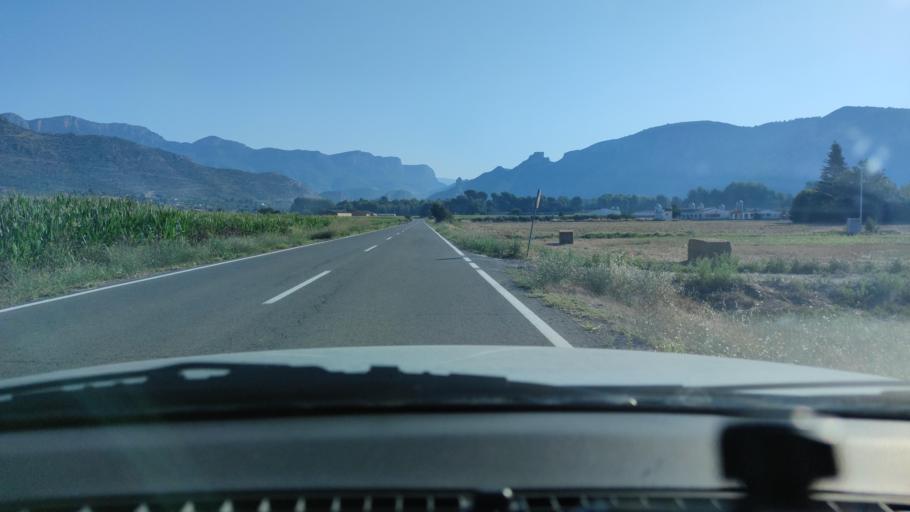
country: ES
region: Catalonia
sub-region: Provincia de Lleida
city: Camarasa
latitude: 41.8510
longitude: 0.8277
